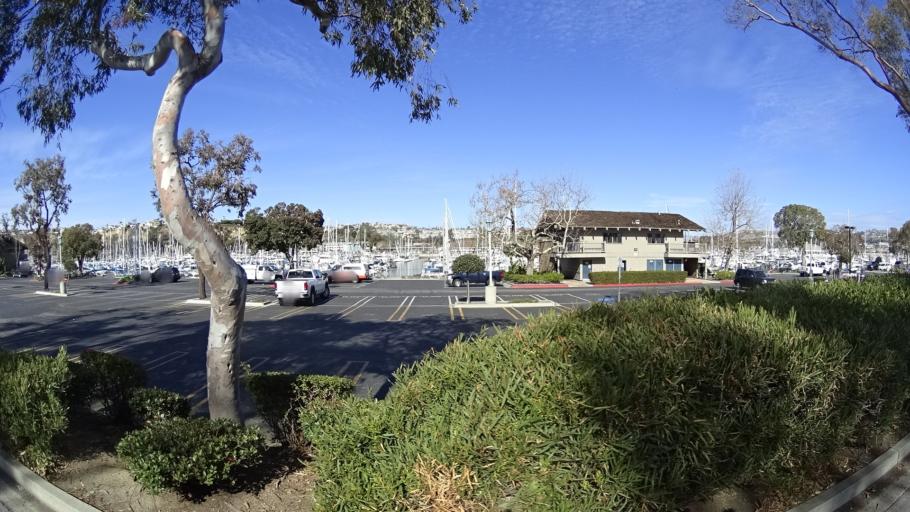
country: US
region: California
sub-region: Orange County
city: Dana Point
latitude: 33.4575
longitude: -117.6971
